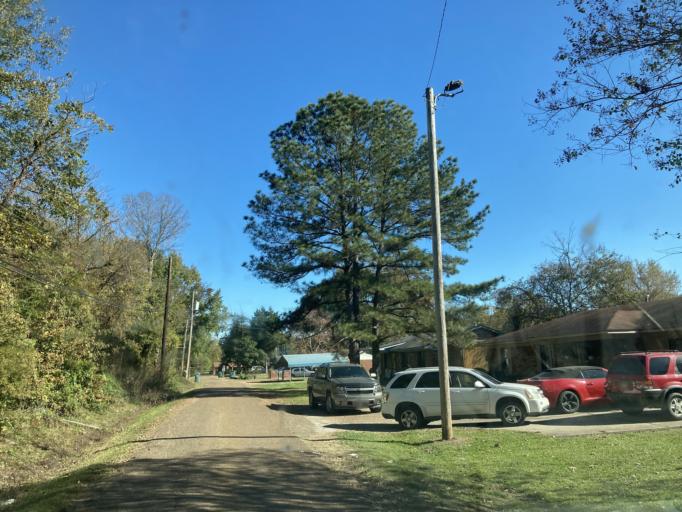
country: US
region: Mississippi
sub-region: Yazoo County
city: Yazoo City
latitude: 32.8434
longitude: -90.4294
